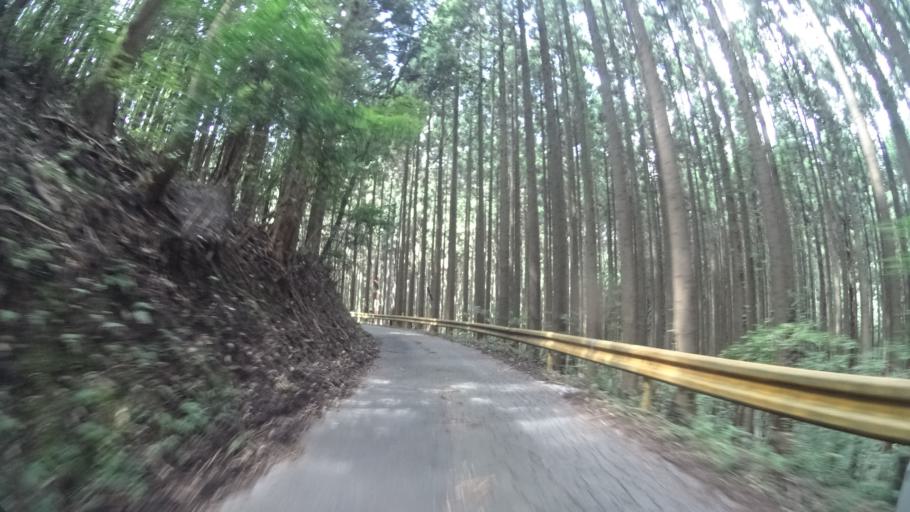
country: JP
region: Yamaguchi
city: Hagi
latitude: 34.4942
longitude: 131.5687
